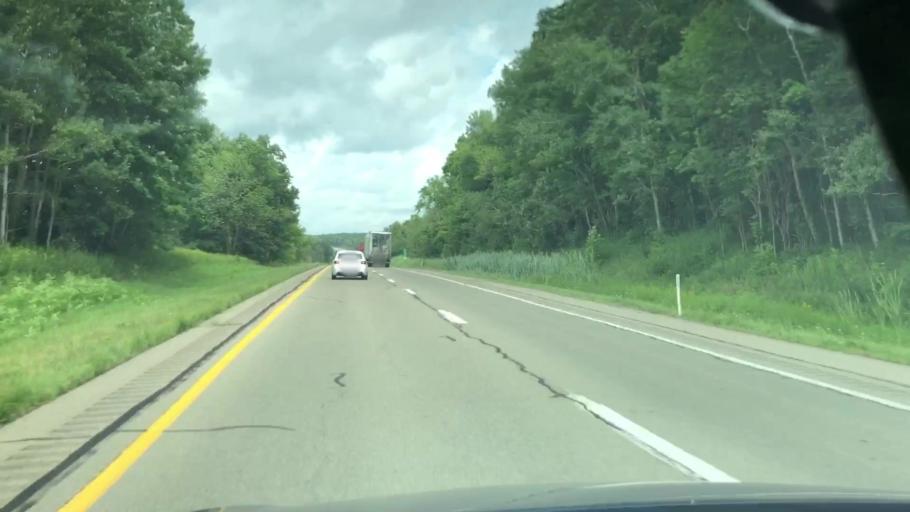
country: US
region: Pennsylvania
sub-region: Erie County
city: Edinboro
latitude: 41.7709
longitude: -80.1903
